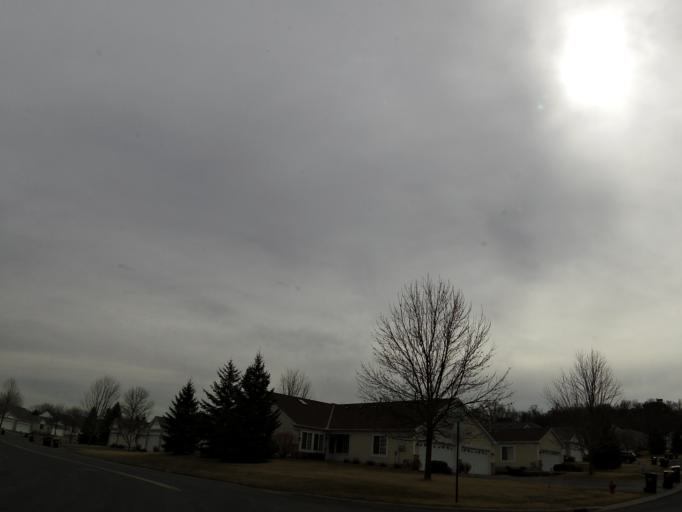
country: US
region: Minnesota
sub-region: Scott County
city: Savage
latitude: 44.7673
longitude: -93.3936
